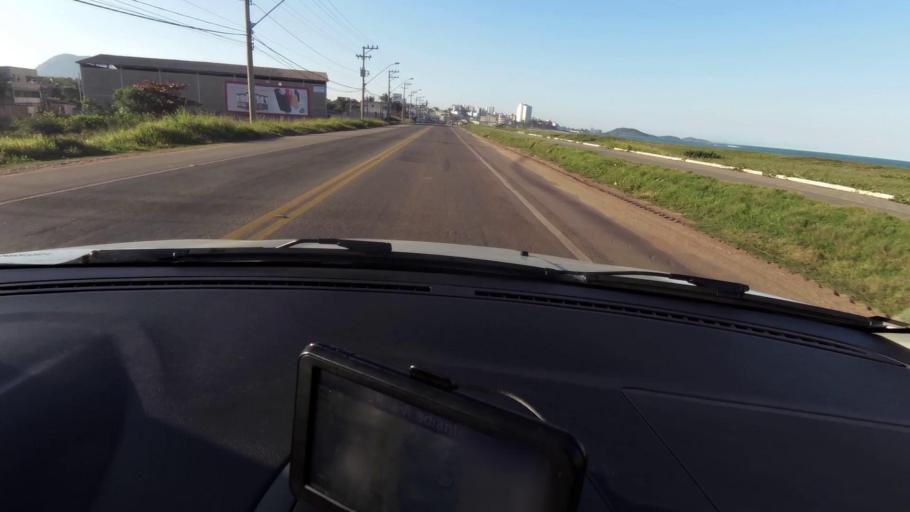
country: BR
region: Espirito Santo
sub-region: Guarapari
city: Guarapari
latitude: -20.6881
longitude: -40.5096
